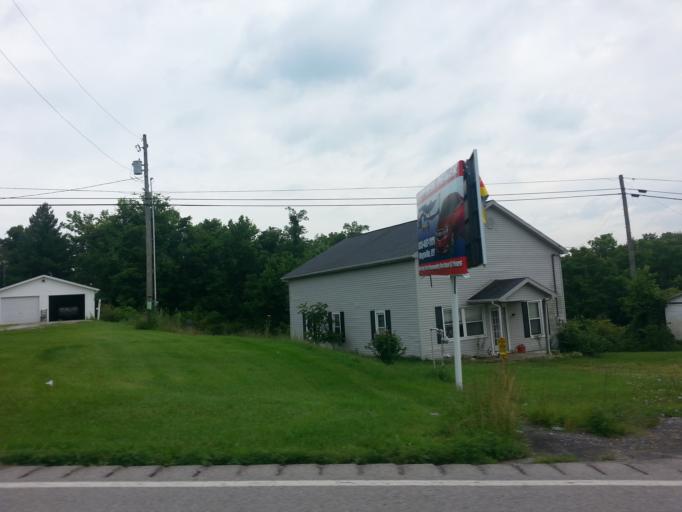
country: US
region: Kentucky
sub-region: Robertson County
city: Mount Olivet
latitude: 38.5325
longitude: -84.0458
